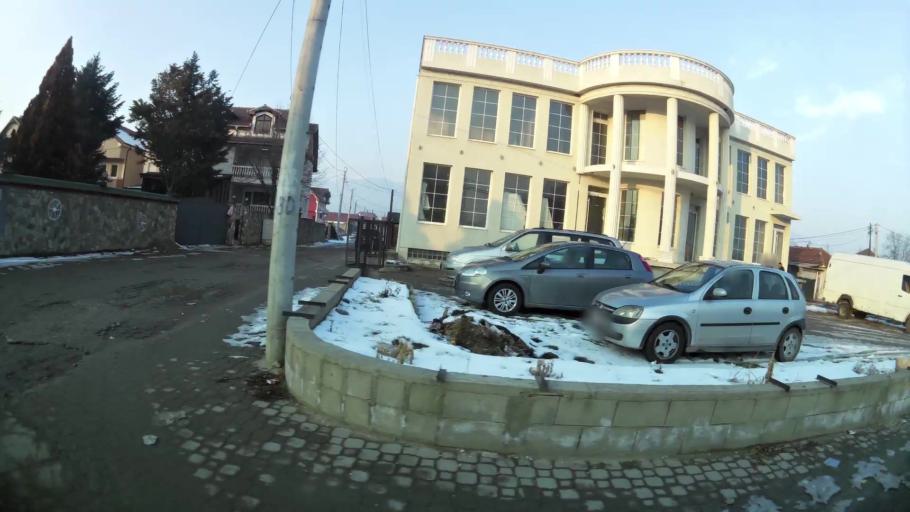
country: MK
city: Creshevo
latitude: 42.0147
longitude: 21.5201
